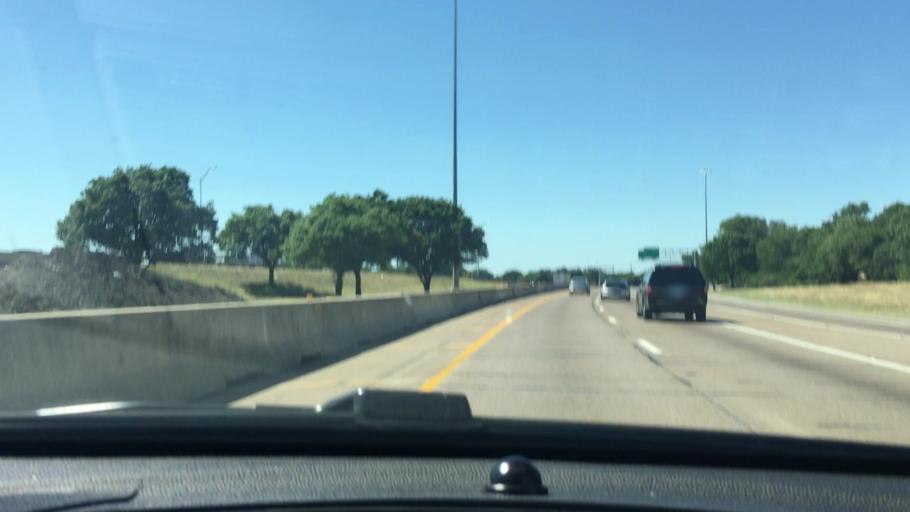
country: US
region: Texas
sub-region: Dallas County
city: Cockrell Hill
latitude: 32.7078
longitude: -96.8288
